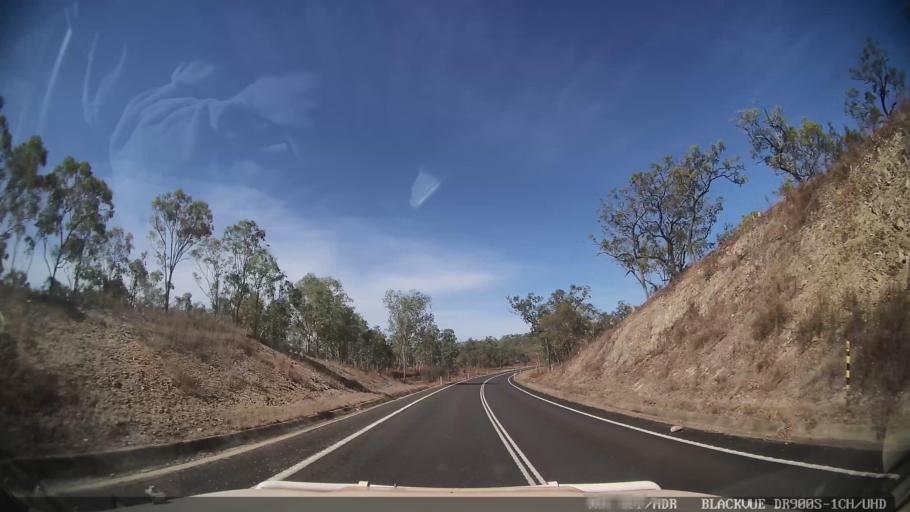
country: AU
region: Queensland
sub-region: Cook
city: Cooktown
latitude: -15.7888
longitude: 144.9397
